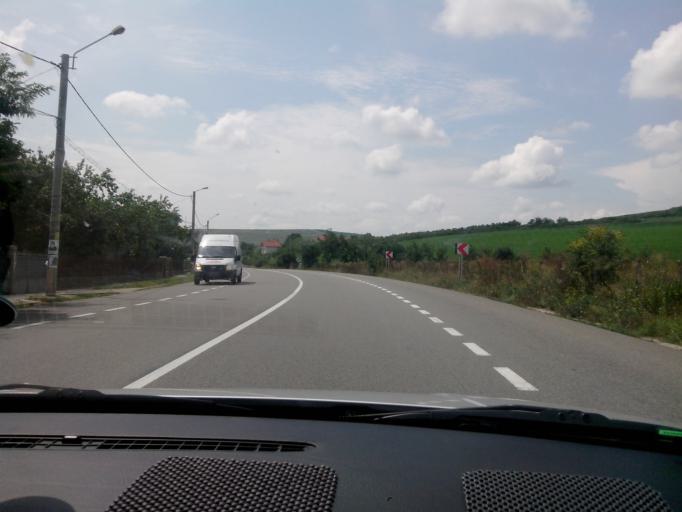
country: RO
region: Cluj
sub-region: Comuna Bontida
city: Rascruci
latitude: 46.9137
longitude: 23.7772
